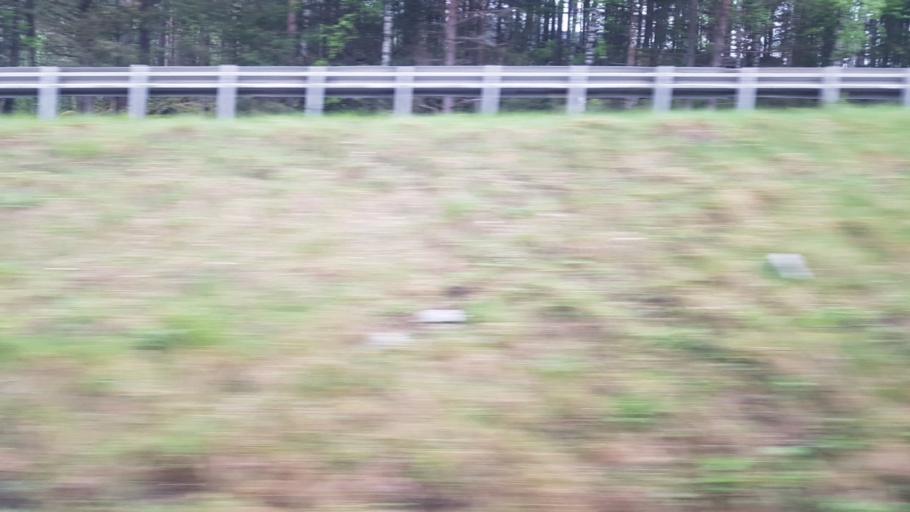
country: NO
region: Oppland
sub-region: Nord-Fron
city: Vinstra
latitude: 61.6062
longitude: 9.7131
